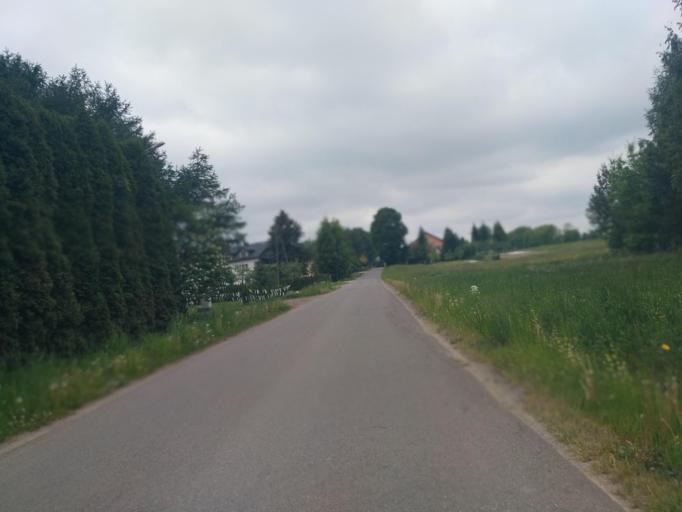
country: PL
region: Subcarpathian Voivodeship
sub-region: Krosno
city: Krosno
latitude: 49.6736
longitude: 21.7386
